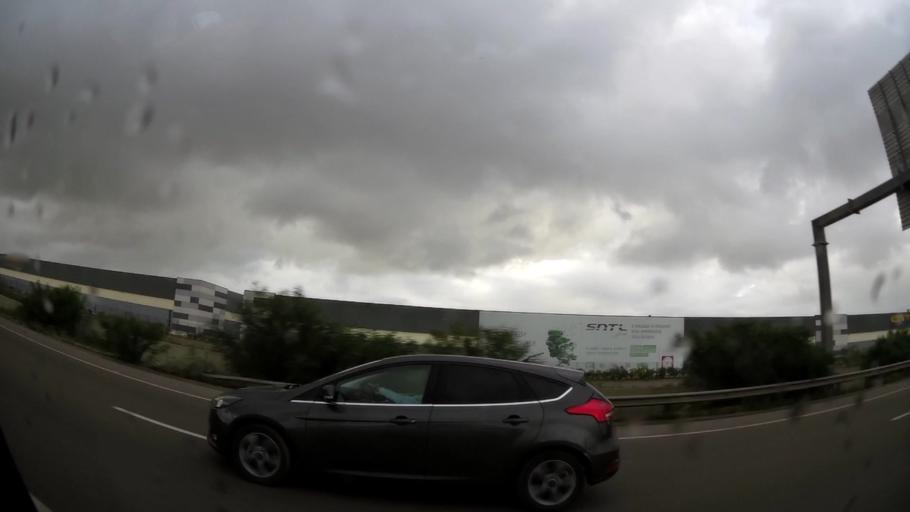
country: MA
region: Grand Casablanca
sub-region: Mohammedia
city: Mohammedia
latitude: 33.6564
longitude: -7.4107
